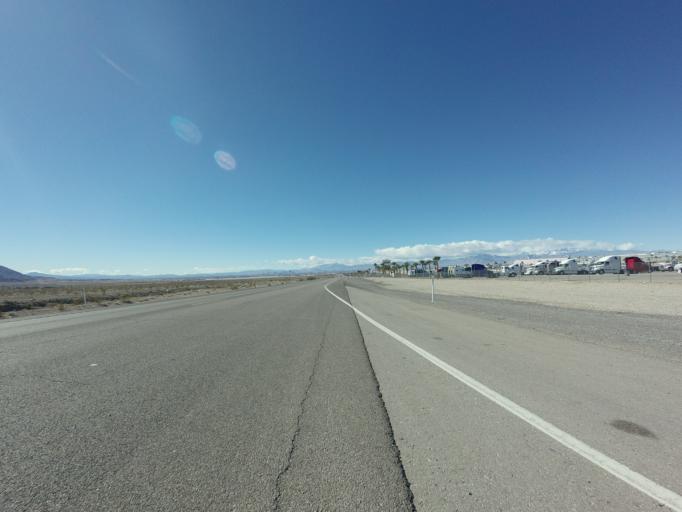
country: US
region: Nevada
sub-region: Clark County
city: Nellis Air Force Base
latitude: 36.2727
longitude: -114.9993
